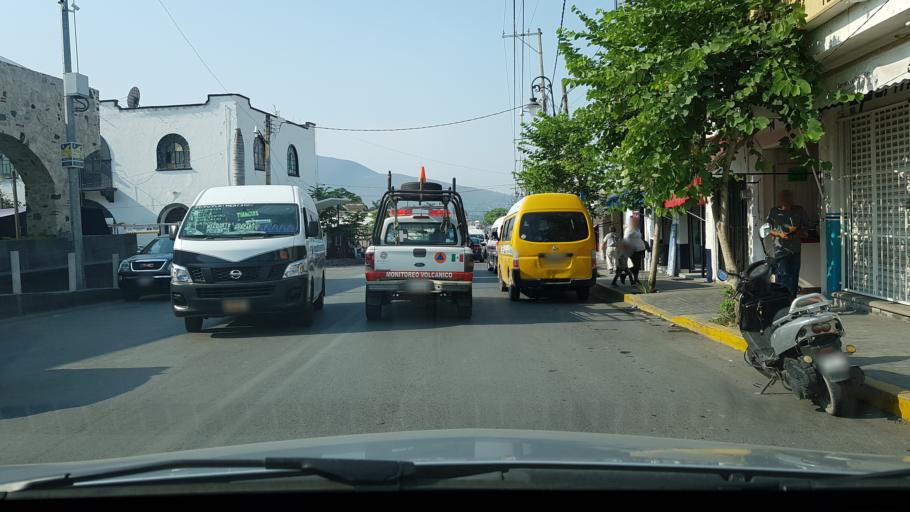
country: MX
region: Morelos
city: Tlaquiltenango
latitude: 18.6303
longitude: -99.1618
